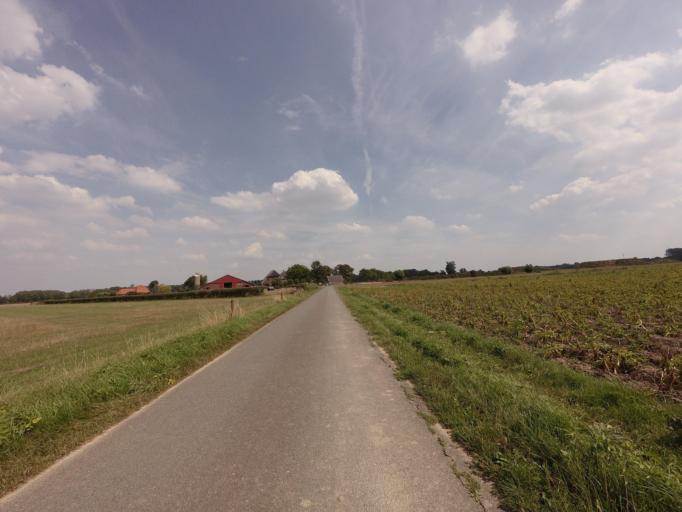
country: NL
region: Gelderland
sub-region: Gemeente Rheden
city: Ellecom
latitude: 52.0052
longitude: 6.0897
